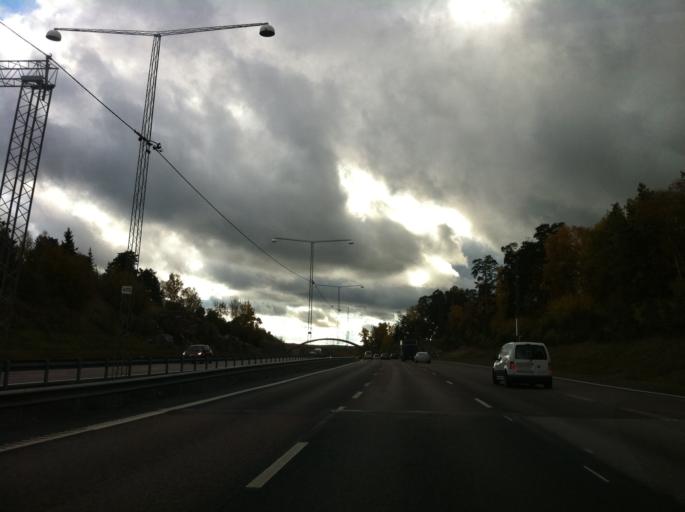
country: SE
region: Stockholm
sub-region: Upplands Vasby Kommun
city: Upplands Vaesby
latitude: 59.4964
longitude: 17.9231
